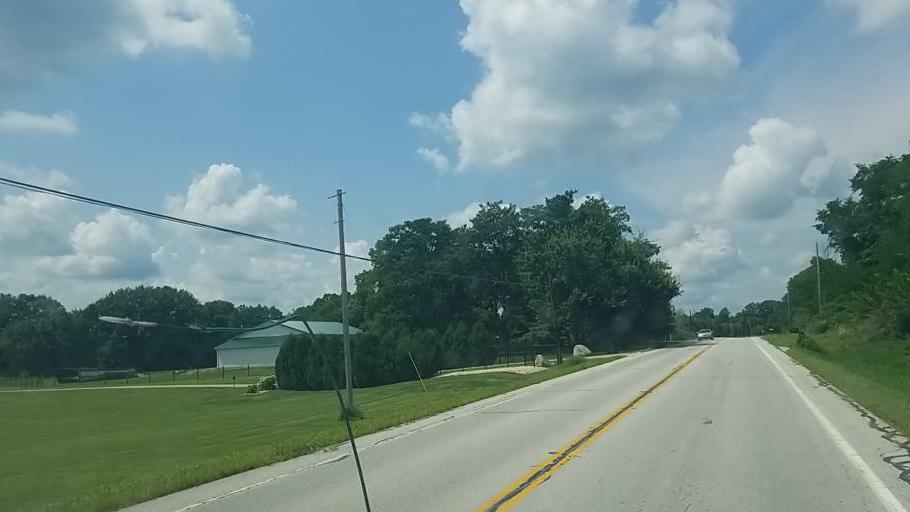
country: US
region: Ohio
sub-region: Medina County
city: Lodi
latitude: 41.0265
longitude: -82.0729
